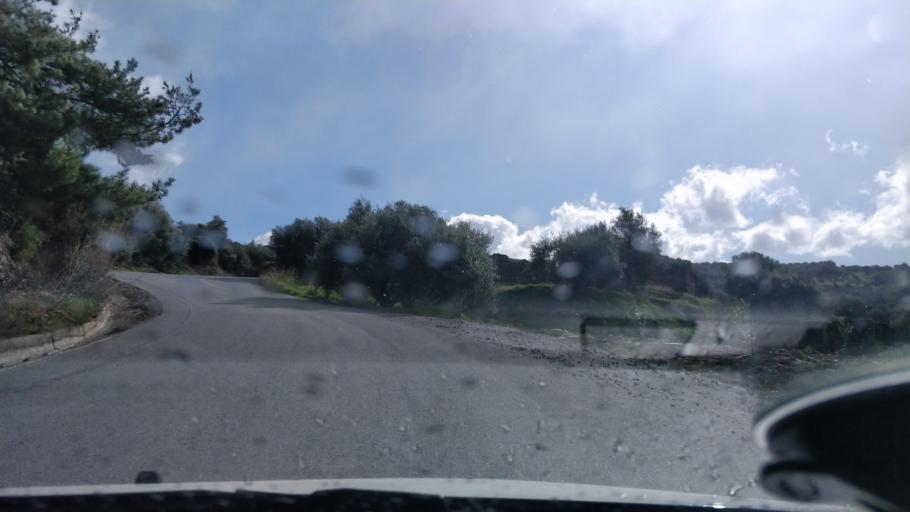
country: GR
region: Crete
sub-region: Nomos Lasithiou
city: Gra Liyia
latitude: 34.9959
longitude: 25.5080
